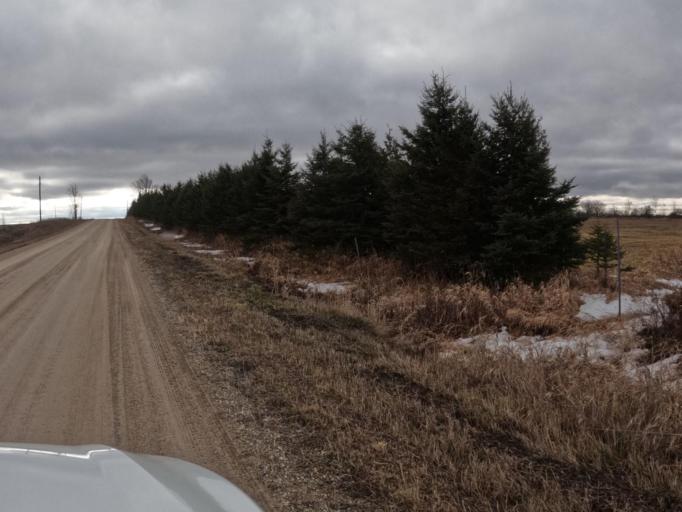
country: CA
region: Ontario
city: Shelburne
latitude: 43.9777
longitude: -80.4043
